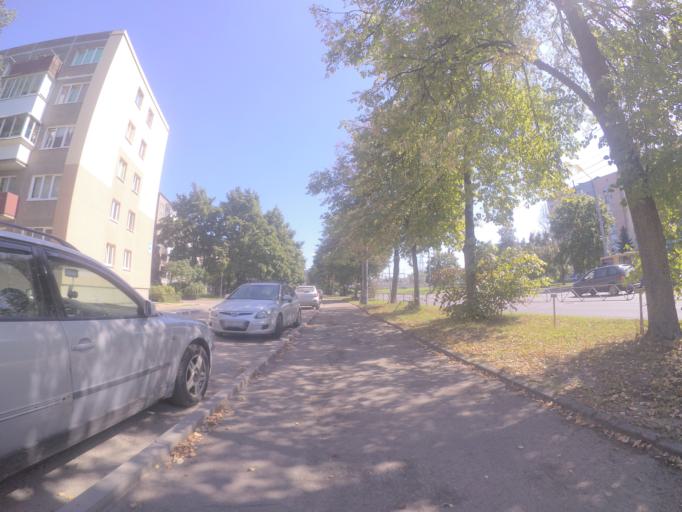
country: BY
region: Grodnenskaya
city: Hrodna
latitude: 53.6645
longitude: 23.7909
